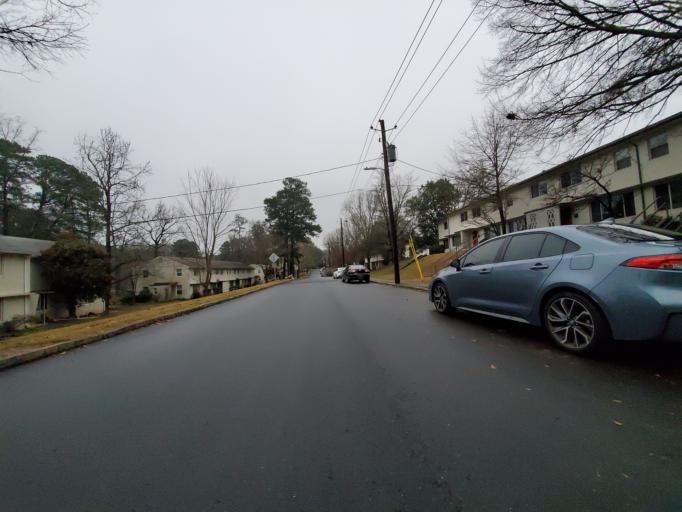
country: US
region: Georgia
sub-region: DeKalb County
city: North Decatur
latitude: 33.7933
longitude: -84.3025
